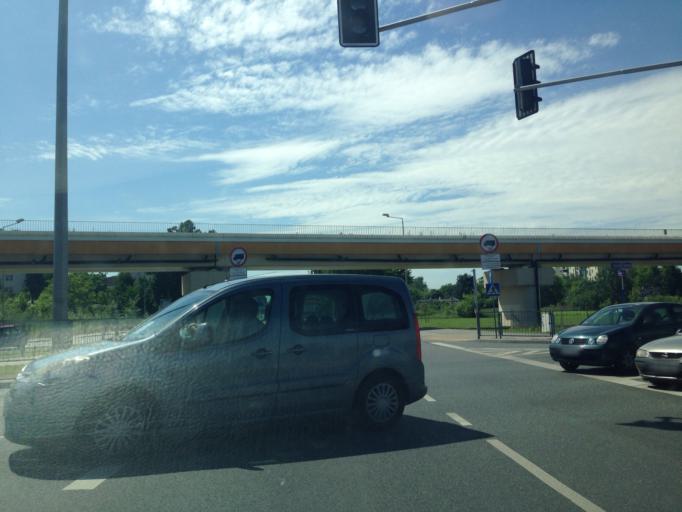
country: PL
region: Masovian Voivodeship
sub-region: Warszawa
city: Bemowo
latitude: 52.2442
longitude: 20.8971
